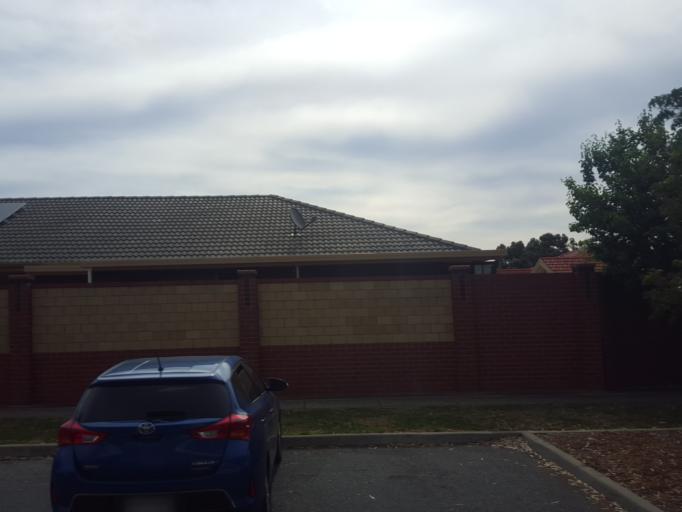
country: AU
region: South Australia
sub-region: Charles Sturt
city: Woodville
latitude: -34.8762
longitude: 138.5548
